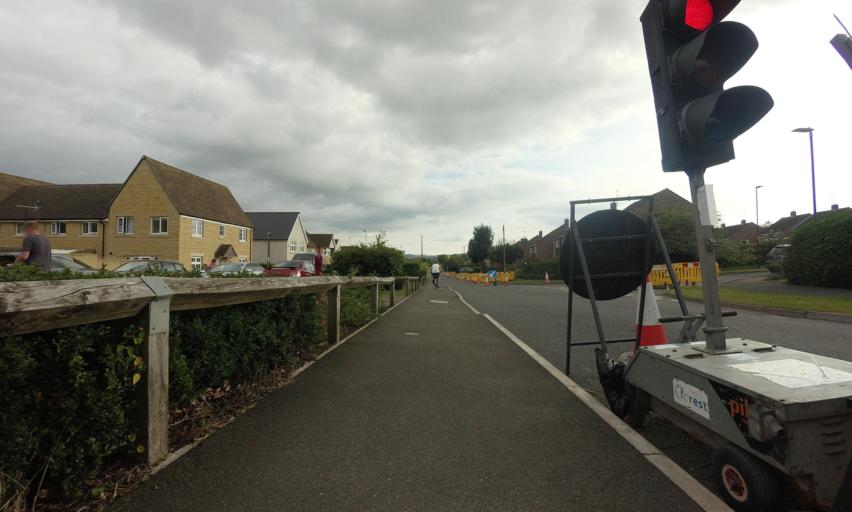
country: GB
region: England
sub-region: Gloucestershire
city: Winchcombe
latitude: 51.9620
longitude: -1.9694
